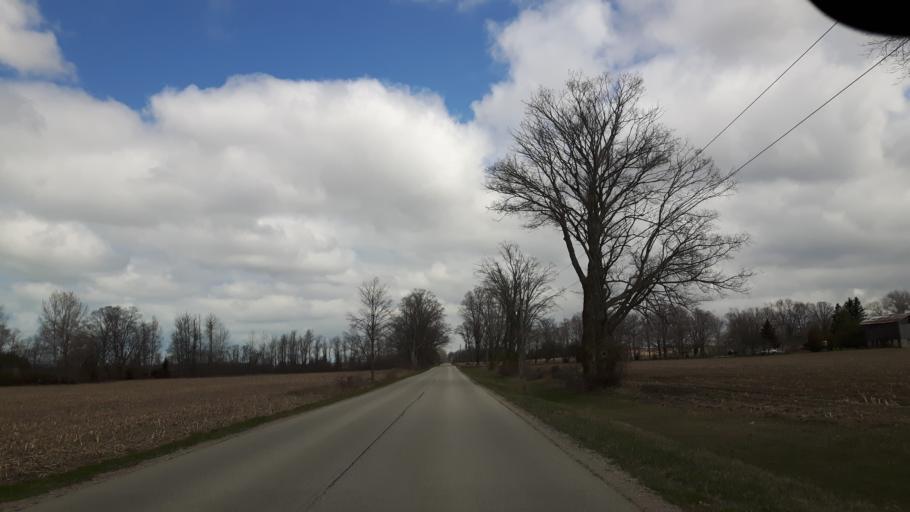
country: CA
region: Ontario
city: Goderich
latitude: 43.6766
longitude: -81.6847
